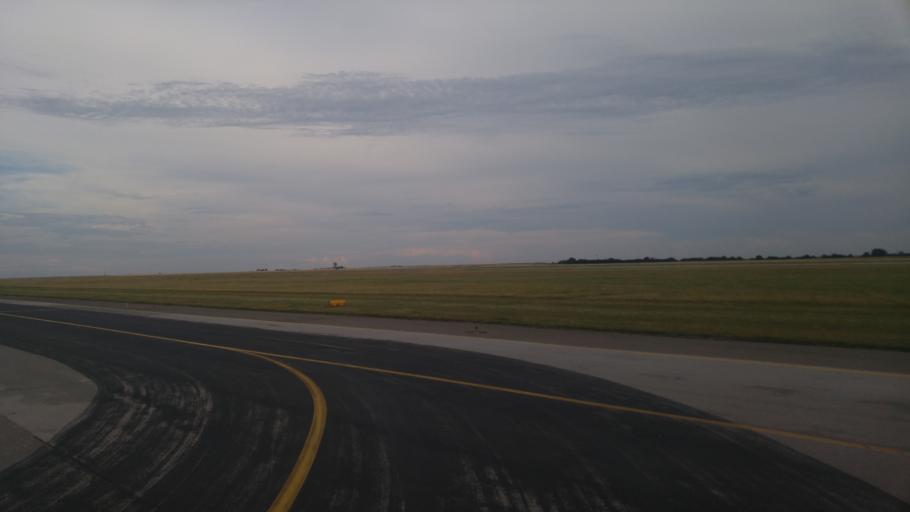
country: CZ
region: Central Bohemia
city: Hostivice
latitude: 50.1045
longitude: 14.2613
